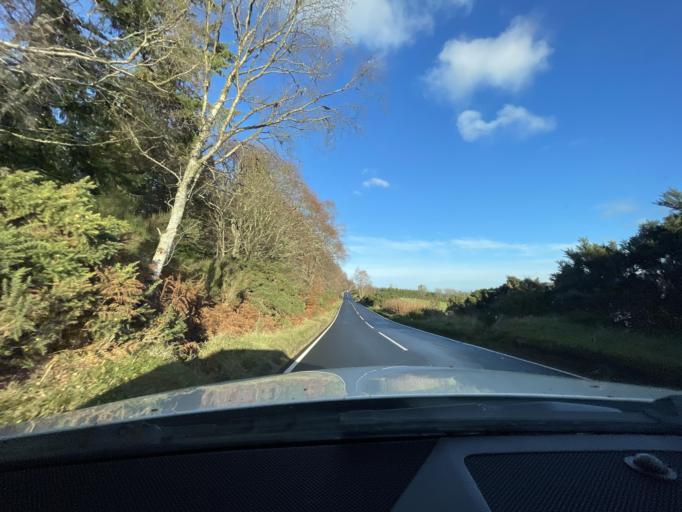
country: GB
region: Scotland
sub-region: Highland
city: Inverness
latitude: 57.4094
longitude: -4.3103
